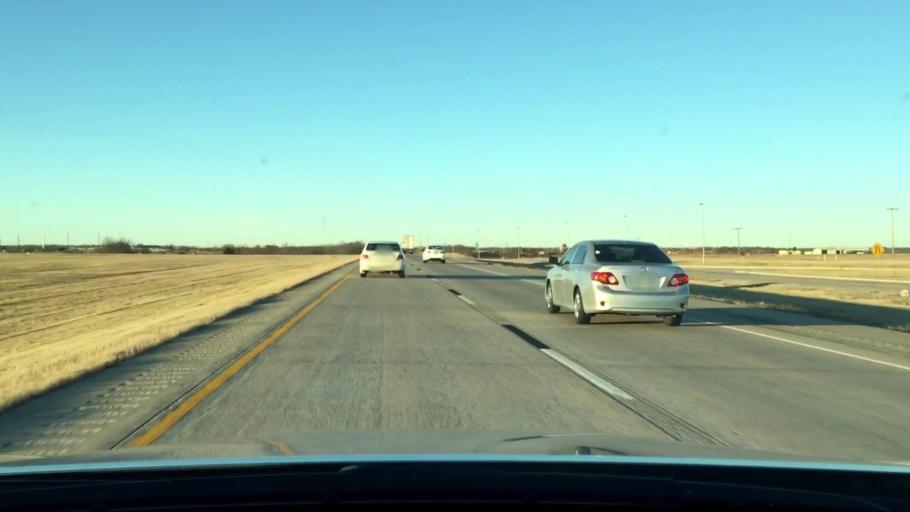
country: US
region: Oklahoma
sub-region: Love County
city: Marietta
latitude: 33.9056
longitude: -97.1341
